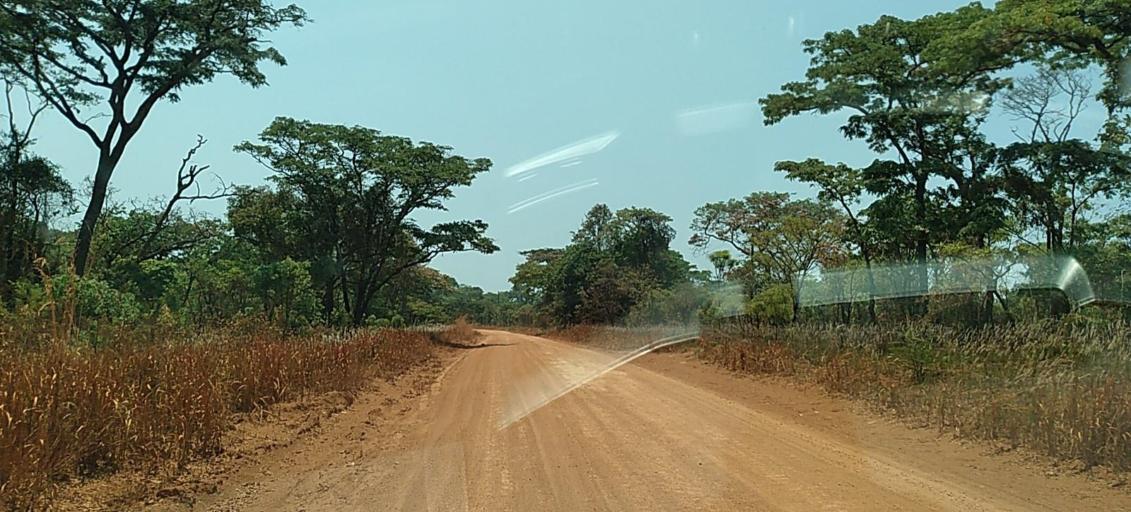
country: CD
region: Katanga
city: Kipushi
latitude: -11.9249
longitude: 27.0111
